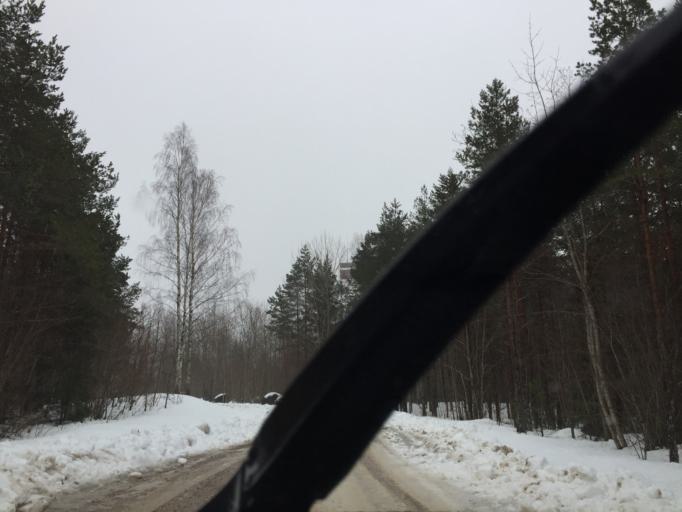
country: EE
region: Saare
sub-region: Kuressaare linn
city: Kuressaare
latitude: 58.2950
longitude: 22.1016
